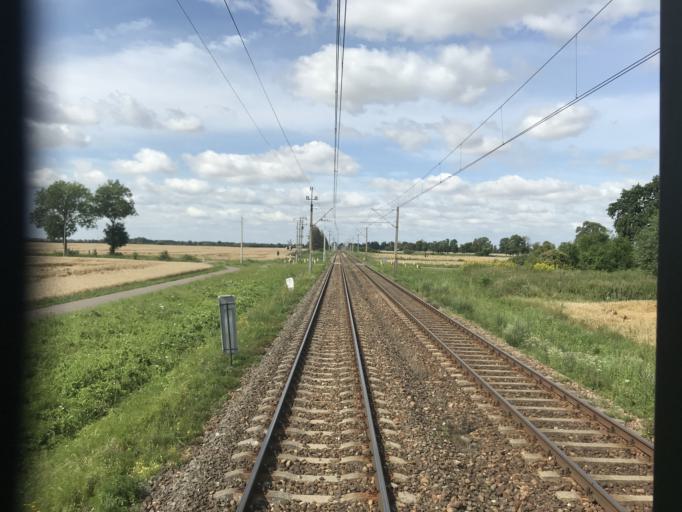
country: PL
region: Pomeranian Voivodeship
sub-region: Powiat malborski
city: Stare Pole
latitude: 54.0485
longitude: 19.1815
